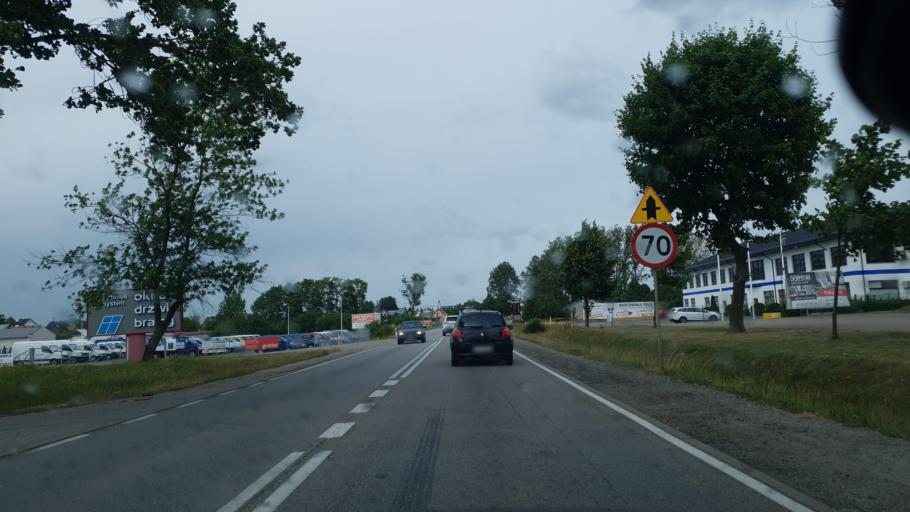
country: PL
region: Pomeranian Voivodeship
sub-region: Powiat kartuski
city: Banino
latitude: 54.4142
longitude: 18.3735
